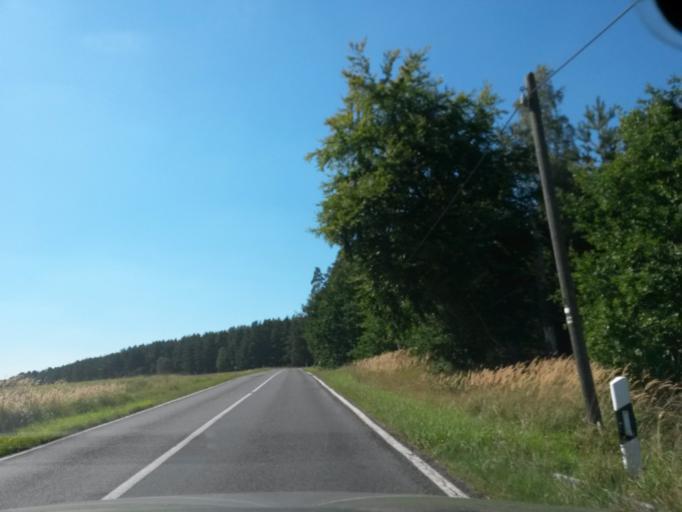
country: DE
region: Brandenburg
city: Lychen
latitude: 53.2328
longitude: 13.3817
